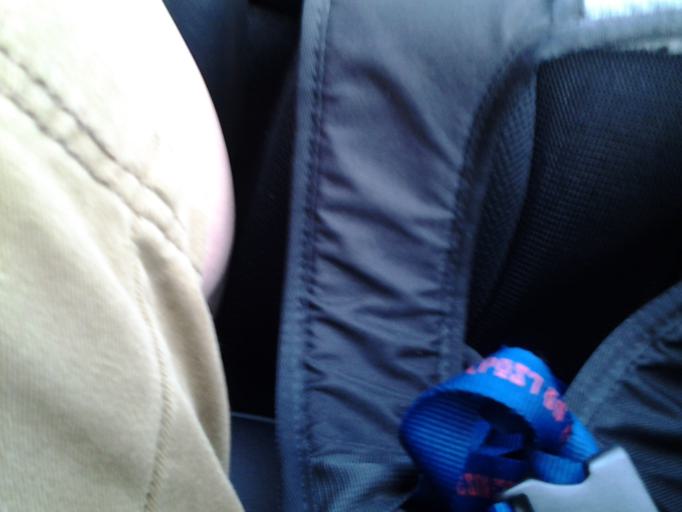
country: DE
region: Schleswig-Holstein
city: Aventoft
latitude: 54.9081
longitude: 8.7655
